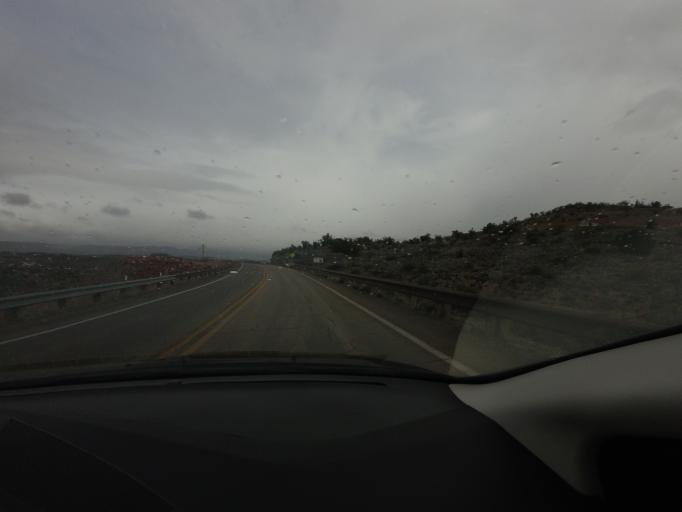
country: US
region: Arizona
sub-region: Yavapai County
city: Lake Montezuma
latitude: 34.6461
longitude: -111.8194
